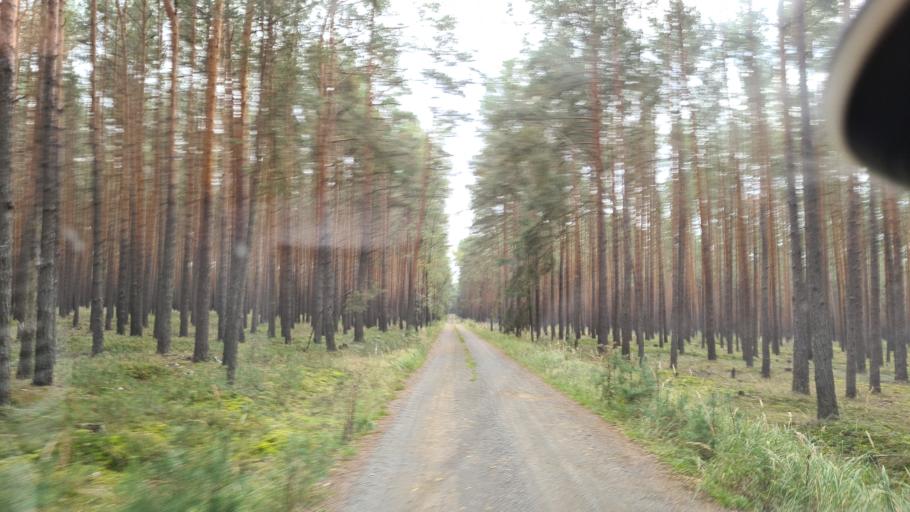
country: DE
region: Brandenburg
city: Schonewalde
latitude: 51.7136
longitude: 13.5768
